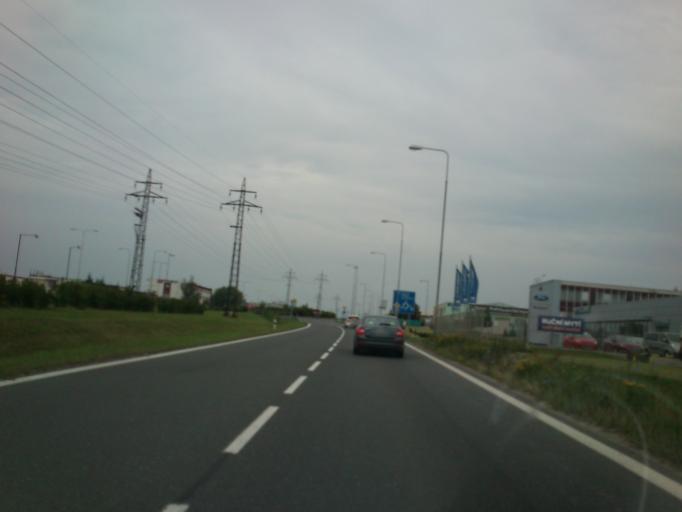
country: CZ
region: Central Bohemia
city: Kosmonosy
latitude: 50.4301
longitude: 14.9330
